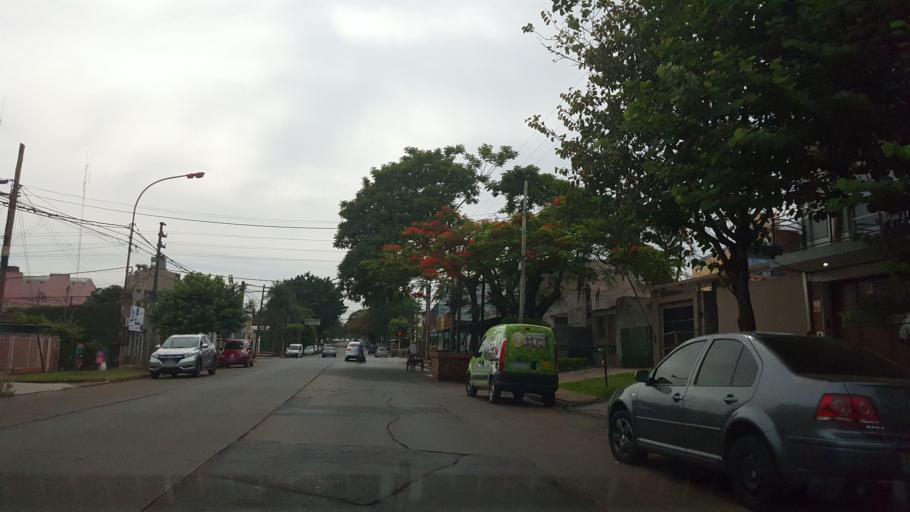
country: AR
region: Misiones
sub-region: Departamento de Capital
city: Posadas
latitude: -27.3698
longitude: -55.9101
